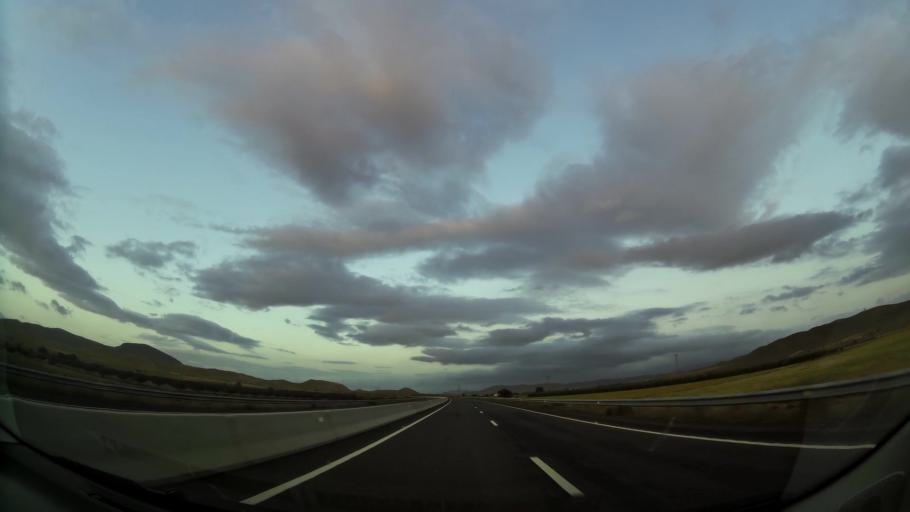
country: MA
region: Oriental
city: El Aioun
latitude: 34.5942
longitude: -2.7021
